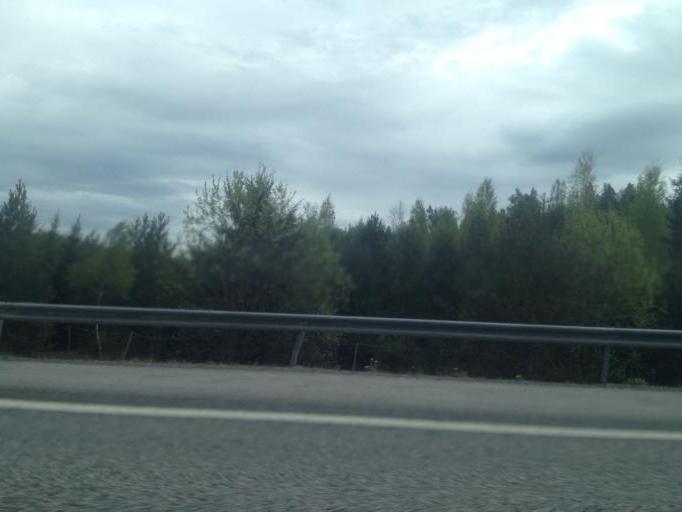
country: FI
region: Uusimaa
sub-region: Helsinki
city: Nurmijaervi
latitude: 60.4049
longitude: 24.8209
